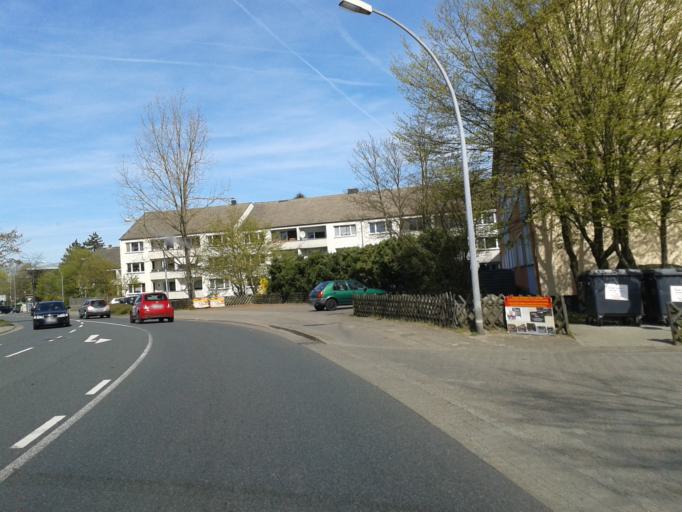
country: DE
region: Lower Saxony
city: Munster
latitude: 52.9856
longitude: 10.0870
